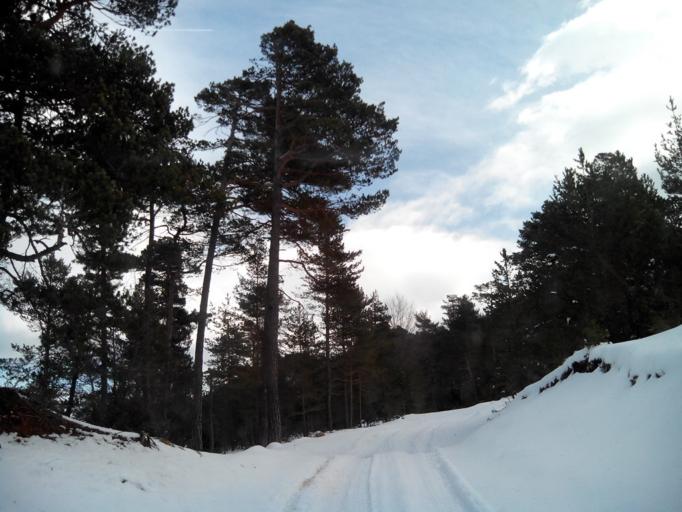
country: ES
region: Catalonia
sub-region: Provincia de Barcelona
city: Sant Julia de Cerdanyola
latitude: 42.2108
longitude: 1.9526
